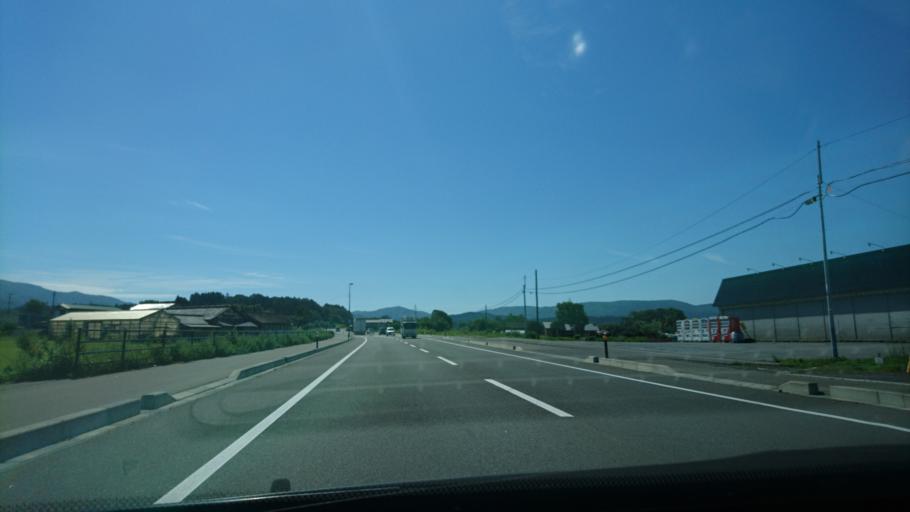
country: JP
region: Iwate
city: Tono
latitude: 39.3096
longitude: 141.5715
